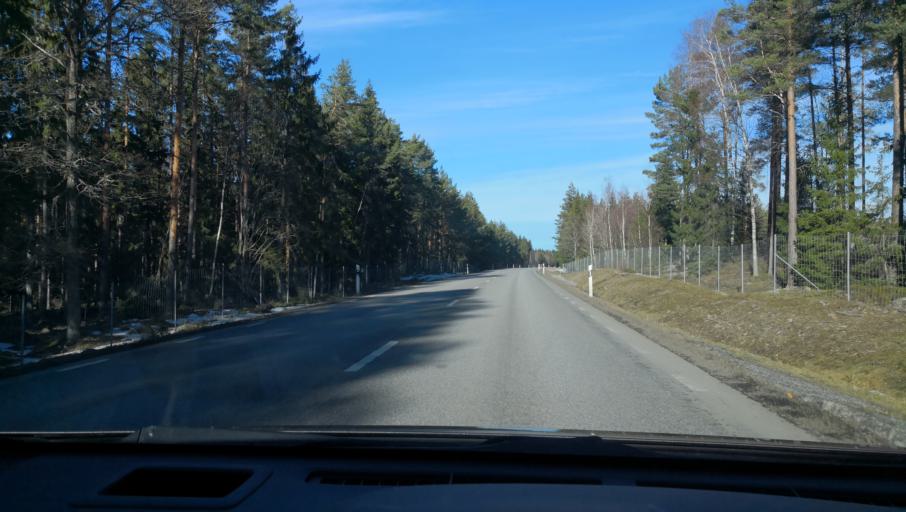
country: SE
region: Uppsala
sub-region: Uppsala Kommun
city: Vattholma
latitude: 60.0468
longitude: 17.7512
